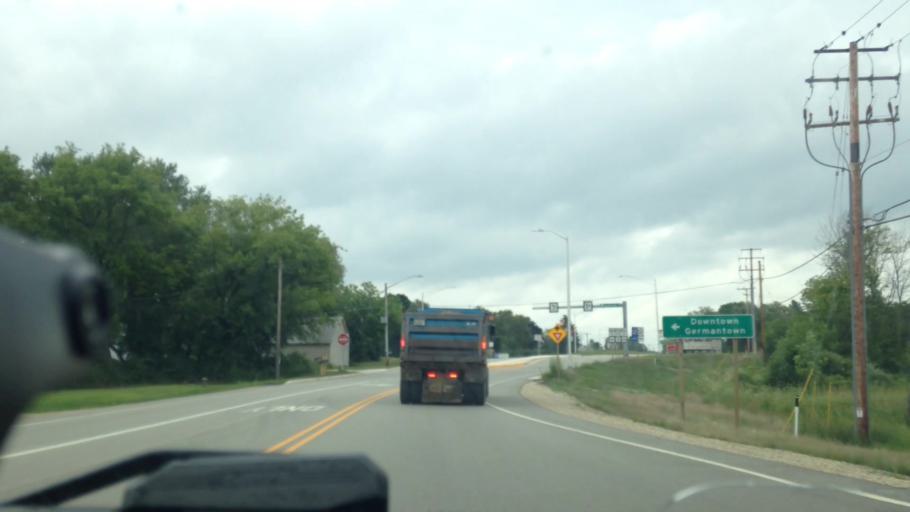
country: US
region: Wisconsin
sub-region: Waukesha County
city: Menomonee Falls
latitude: 43.2071
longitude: -88.1589
